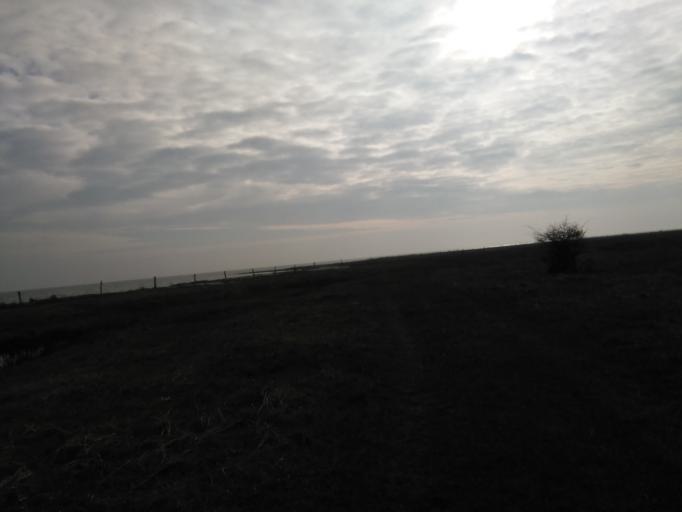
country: DK
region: Central Jutland
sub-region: Odder Kommune
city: Odder
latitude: 55.8384
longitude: 10.1943
